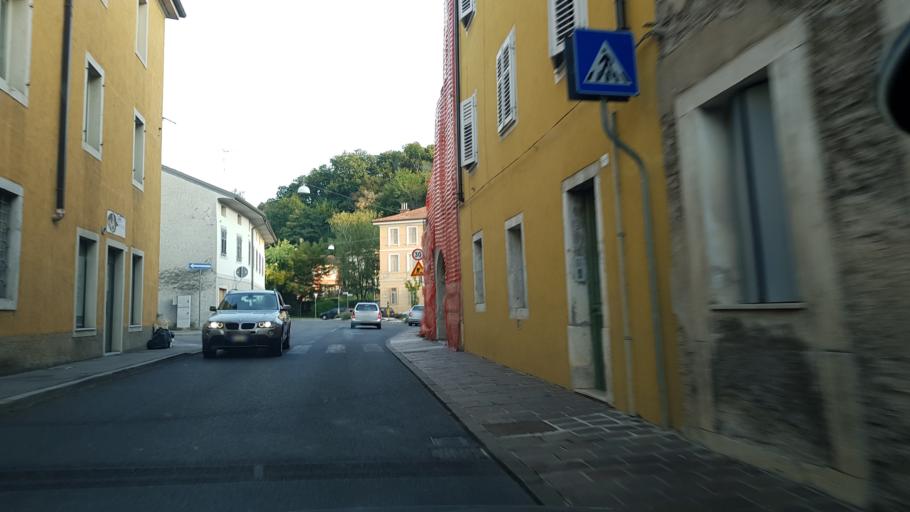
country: IT
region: Friuli Venezia Giulia
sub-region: Provincia di Gorizia
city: Gorizia
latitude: 45.9484
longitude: 13.6298
